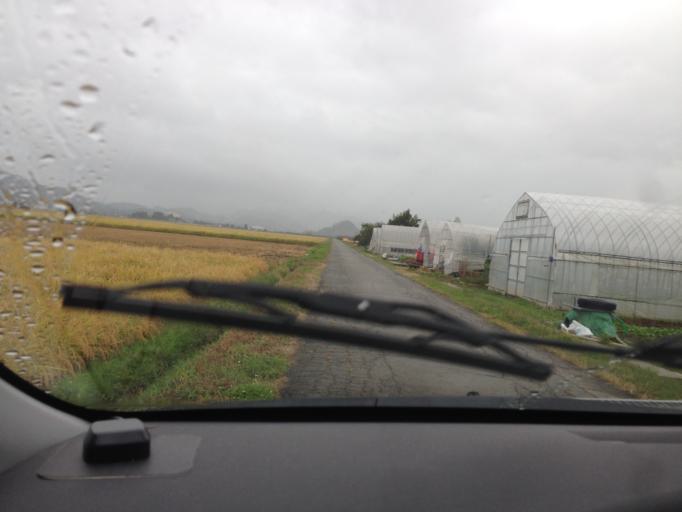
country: JP
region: Fukushima
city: Kitakata
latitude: 37.4710
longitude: 139.8734
